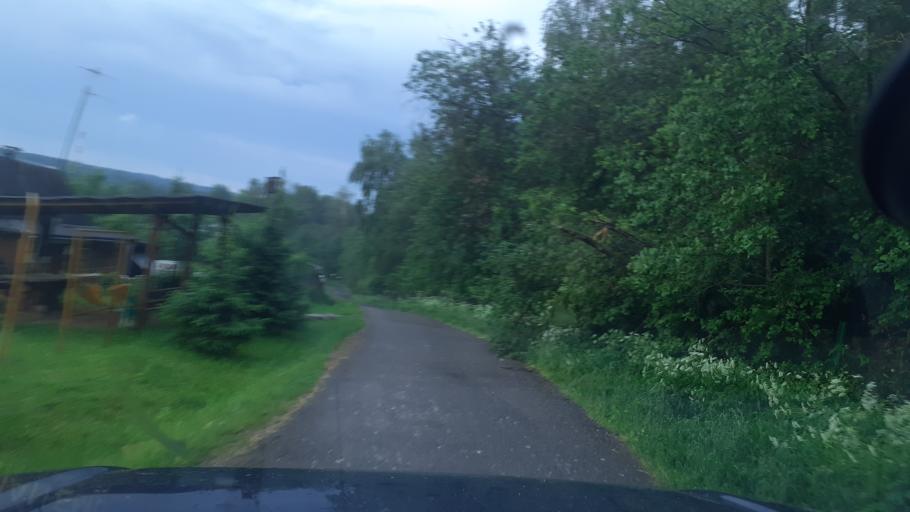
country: RU
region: Moskovskaya
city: Ateptsevo
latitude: 55.3042
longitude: 36.7639
